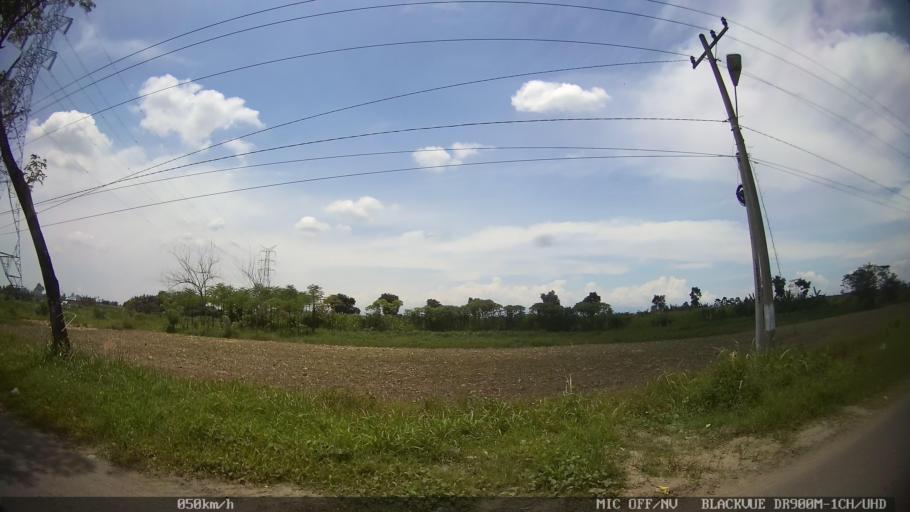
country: ID
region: North Sumatra
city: Binjai
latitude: 3.5907
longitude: 98.5125
